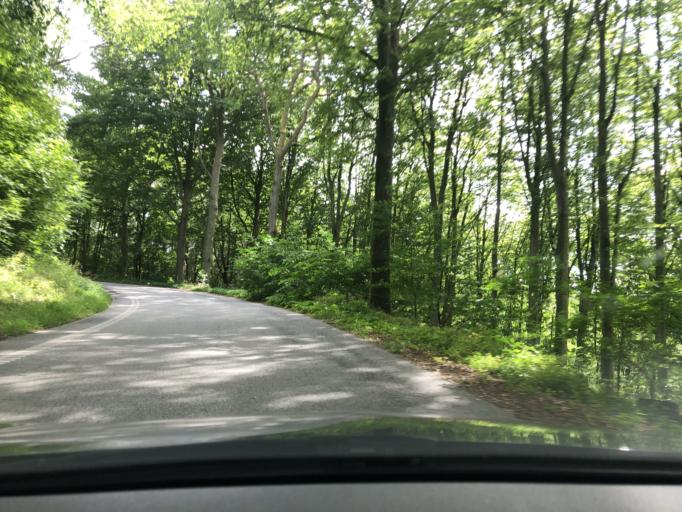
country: DK
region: South Denmark
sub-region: Vejle Kommune
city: Jelling
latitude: 55.6995
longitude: 9.4424
